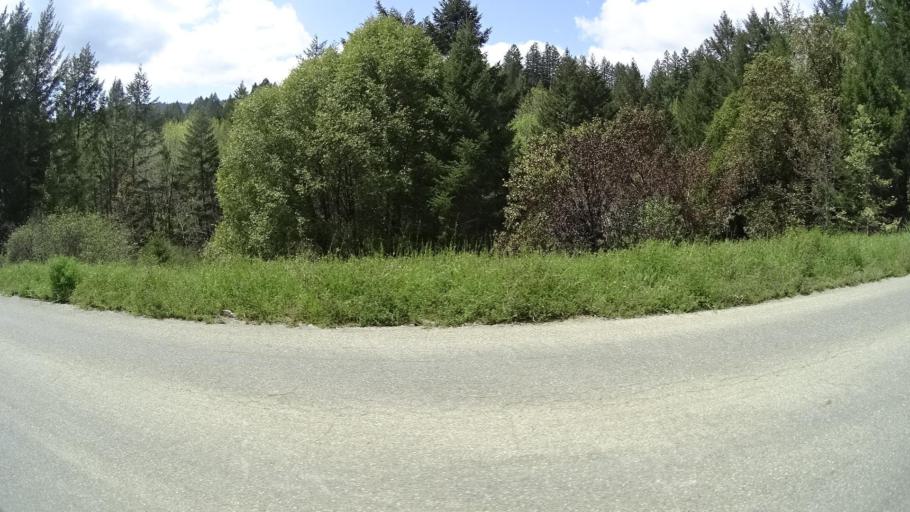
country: US
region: California
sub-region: Humboldt County
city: Redway
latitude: 40.1003
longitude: -123.9263
